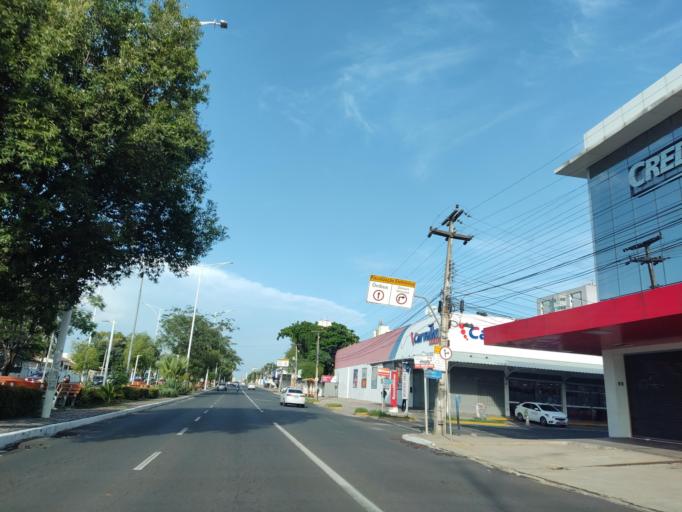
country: BR
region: Piaui
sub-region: Teresina
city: Teresina
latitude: -5.0861
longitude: -42.8021
